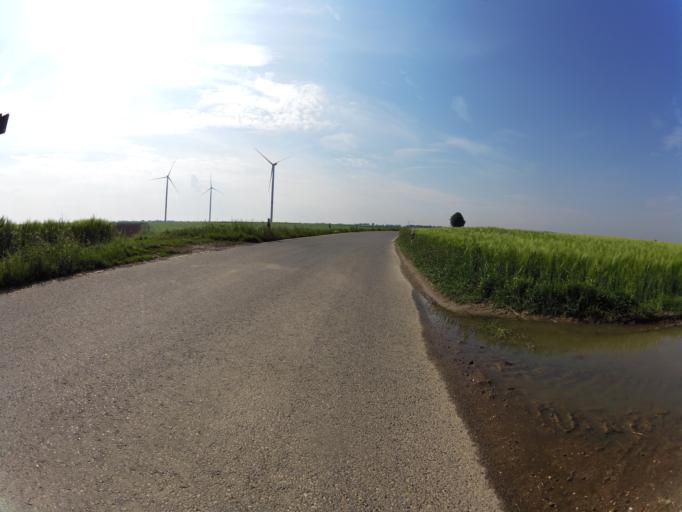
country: DE
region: North Rhine-Westphalia
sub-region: Regierungsbezirk Koln
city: Gangelt
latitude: 51.0347
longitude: 6.0400
